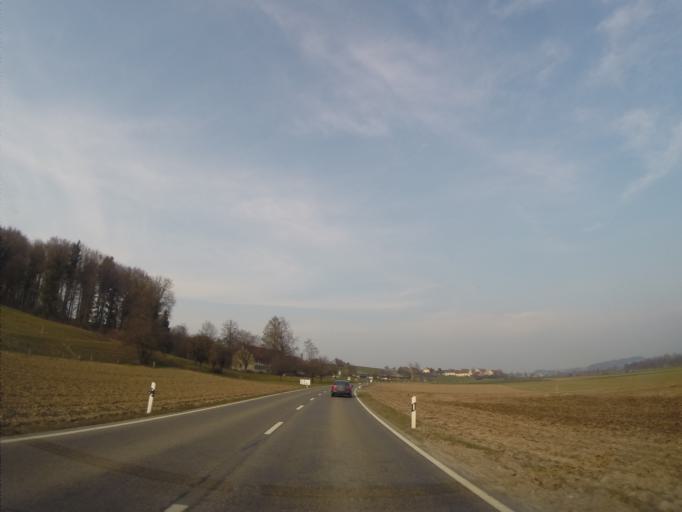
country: CH
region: Zurich
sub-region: Bezirk Winterthur
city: Neftenbach / Dorf Neftenbach
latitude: 47.5361
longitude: 8.6711
